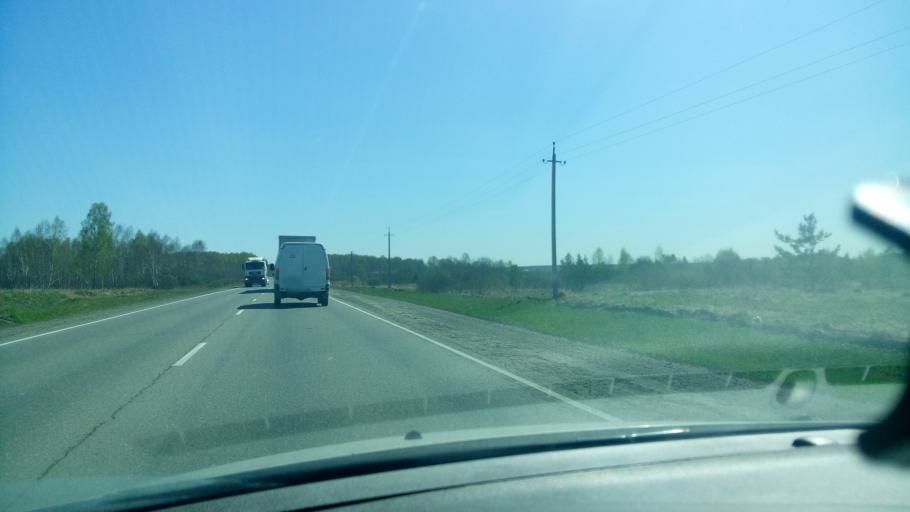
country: RU
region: Sverdlovsk
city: Bogdanovich
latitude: 56.7546
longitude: 62.1886
